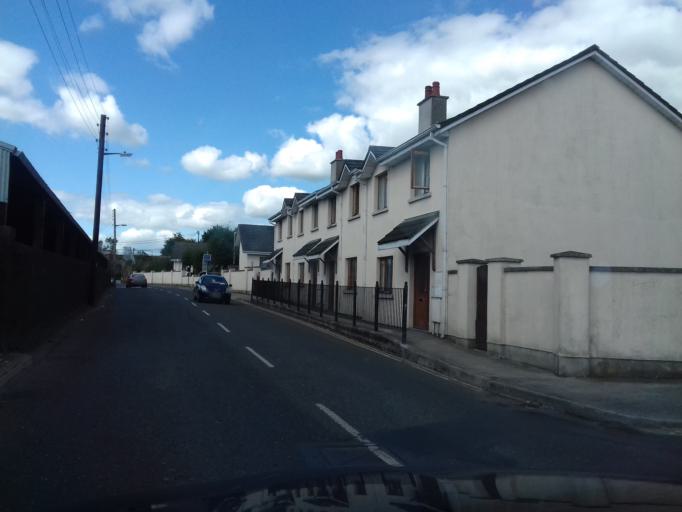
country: IE
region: Munster
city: Carrick-on-Suir
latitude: 52.3502
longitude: -7.4152
